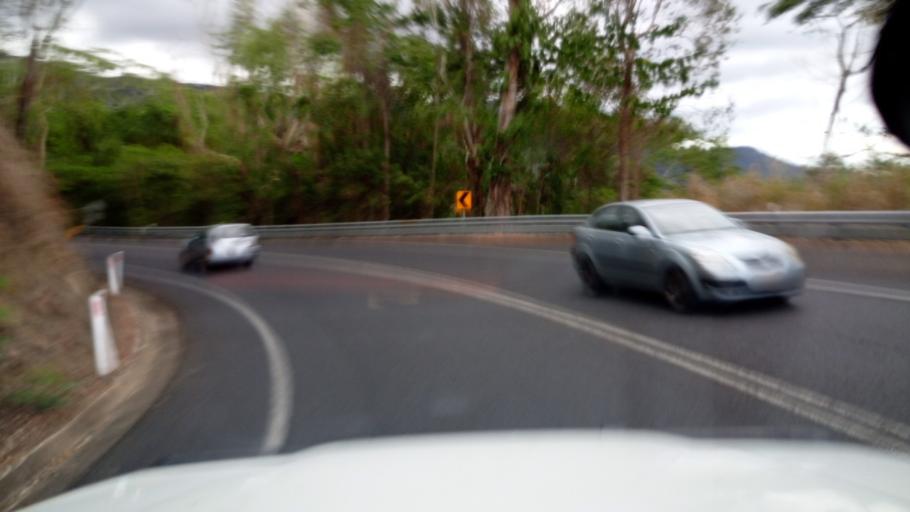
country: AU
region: Queensland
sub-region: Cairns
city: Redlynch
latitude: -16.8507
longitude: 145.6874
